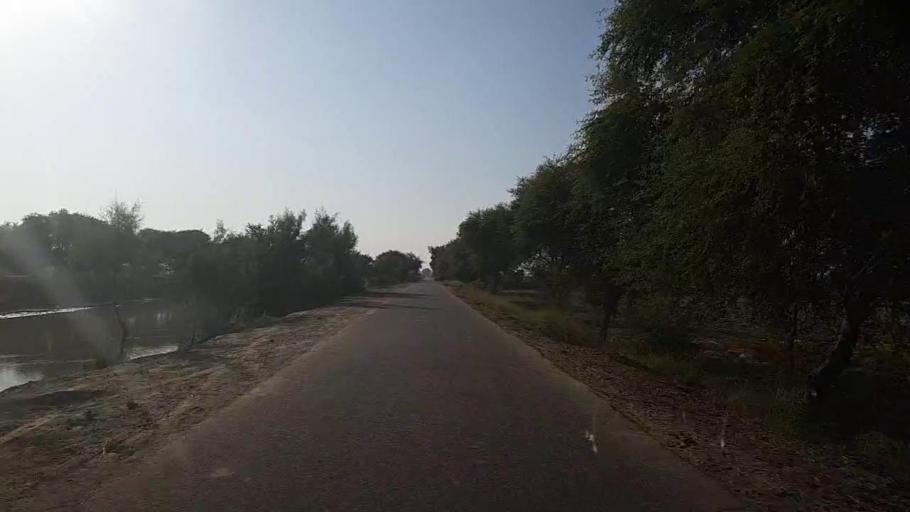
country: PK
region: Sindh
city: Tangwani
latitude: 28.3011
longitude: 68.9433
